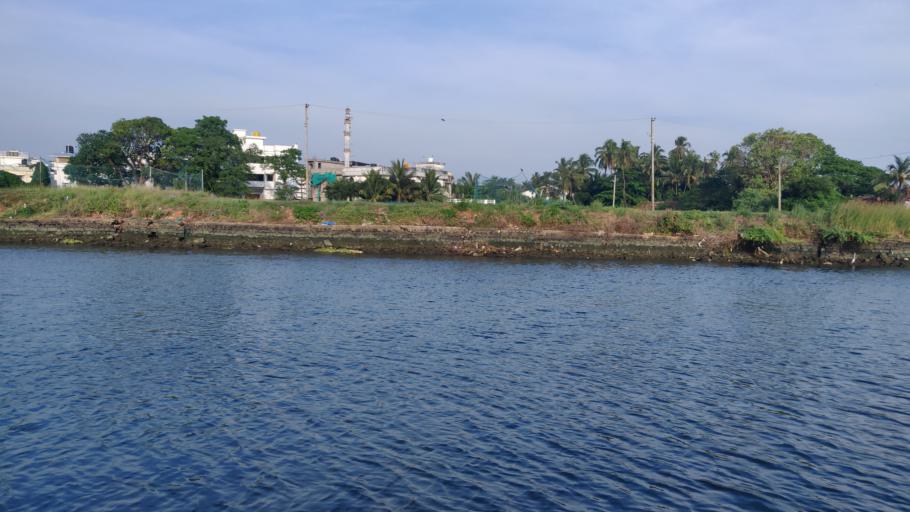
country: IN
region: Karnataka
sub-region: Dakshina Kannada
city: Mangalore
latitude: 12.8712
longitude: 74.8292
